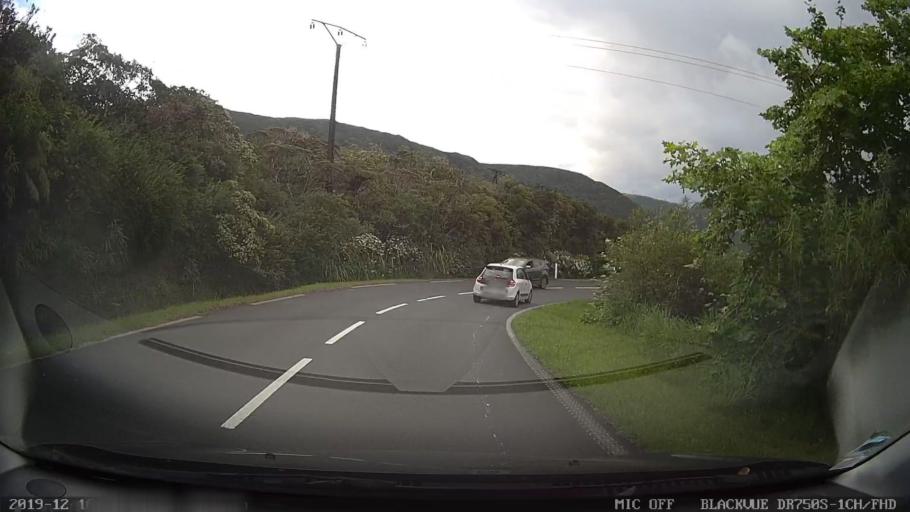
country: RE
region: Reunion
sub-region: Reunion
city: Cilaos
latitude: -21.1586
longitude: 55.5970
